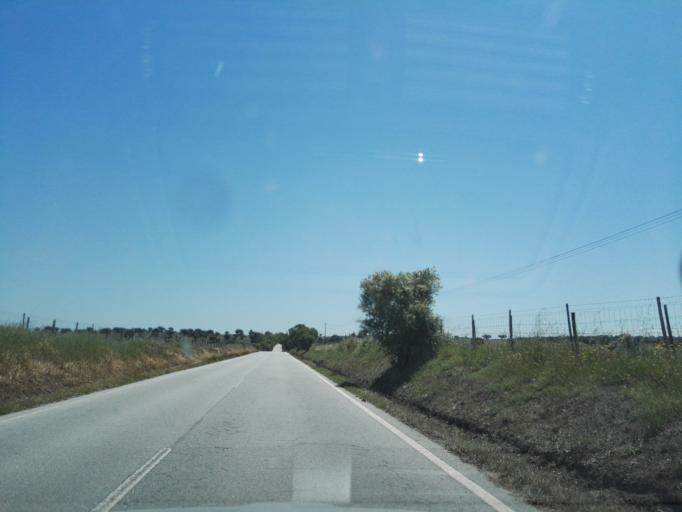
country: PT
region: Portalegre
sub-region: Arronches
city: Arronches
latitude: 39.0083
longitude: -7.2372
